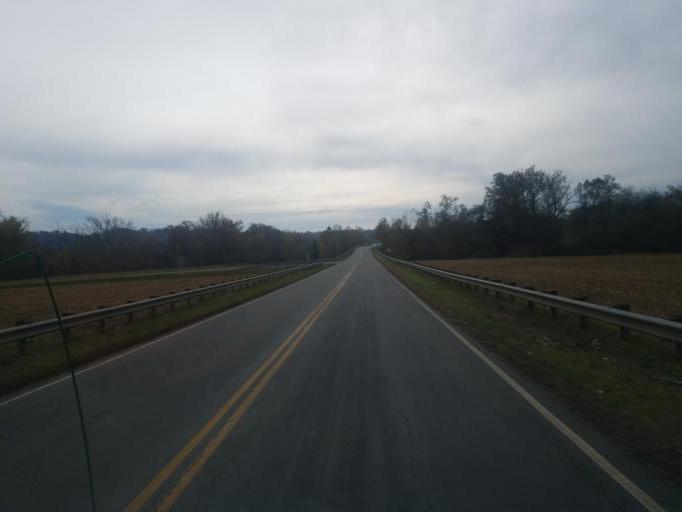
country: US
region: Ohio
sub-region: Washington County
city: Beverly
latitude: 39.5473
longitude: -81.6463
